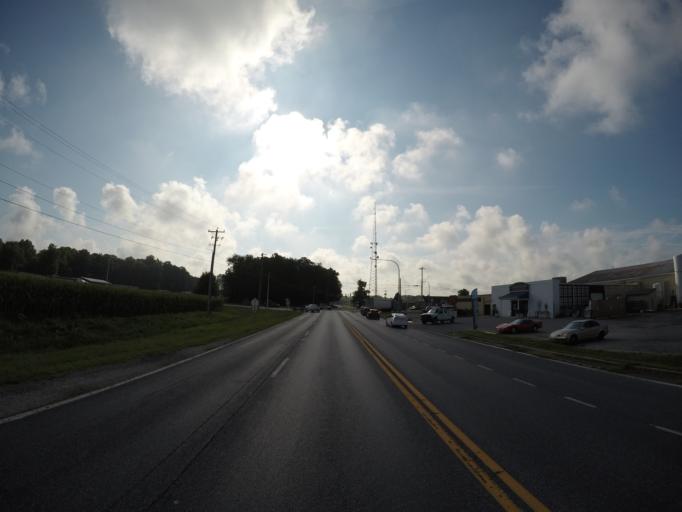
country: US
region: Delaware
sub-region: Sussex County
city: Bridgeville
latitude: 38.7598
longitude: -75.5948
